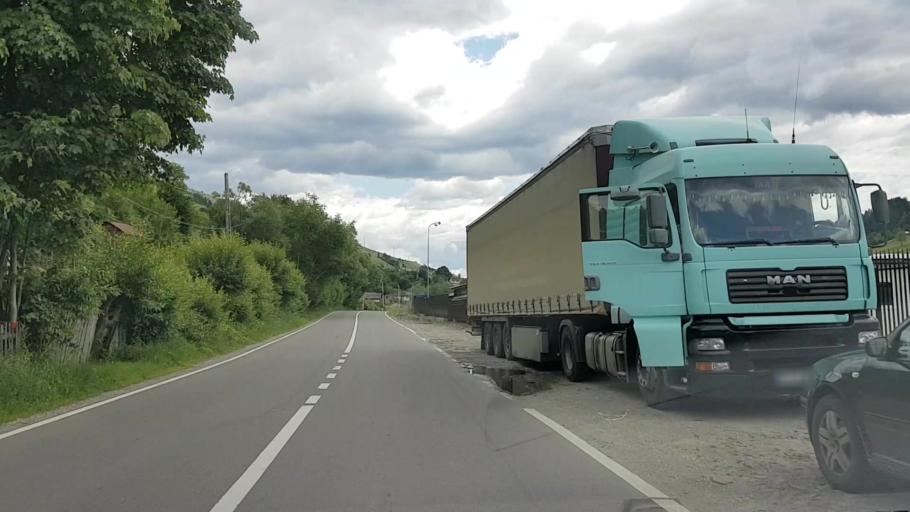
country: RO
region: Neamt
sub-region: Comuna Borca
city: Borca
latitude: 47.1704
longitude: 25.7975
